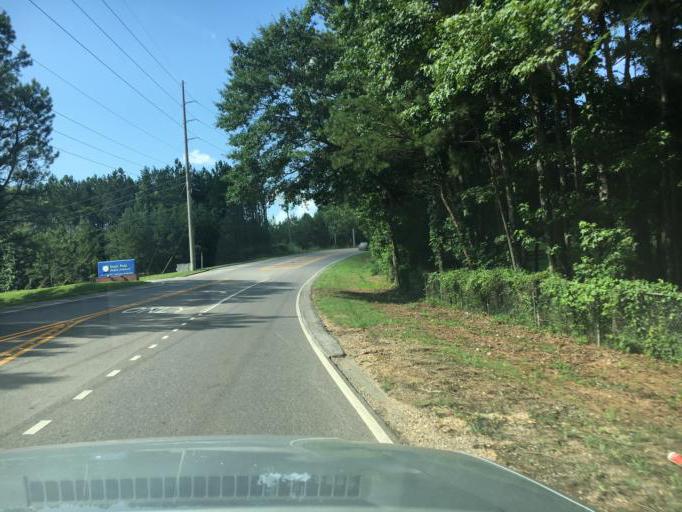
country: US
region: Alabama
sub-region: Shelby County
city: Meadowbrook
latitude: 33.3932
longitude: -86.7213
